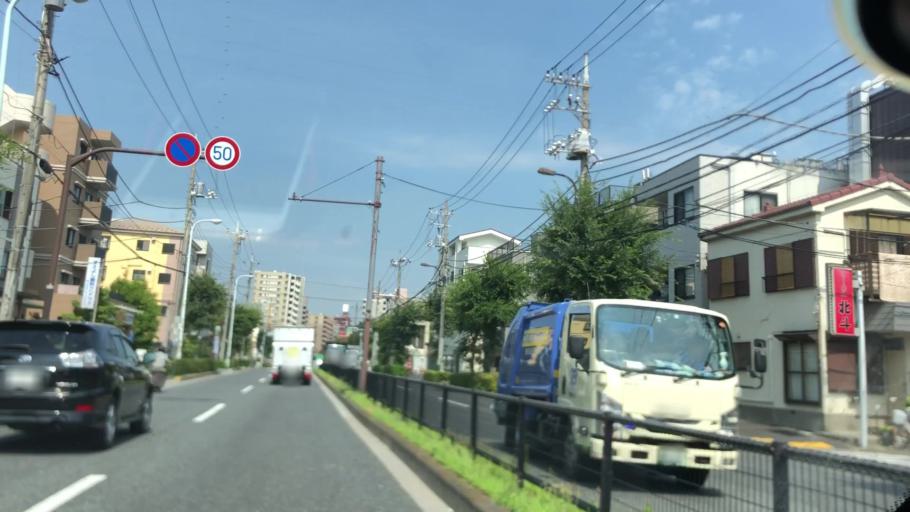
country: JP
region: Tokyo
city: Urayasu
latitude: 35.6839
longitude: 139.8734
